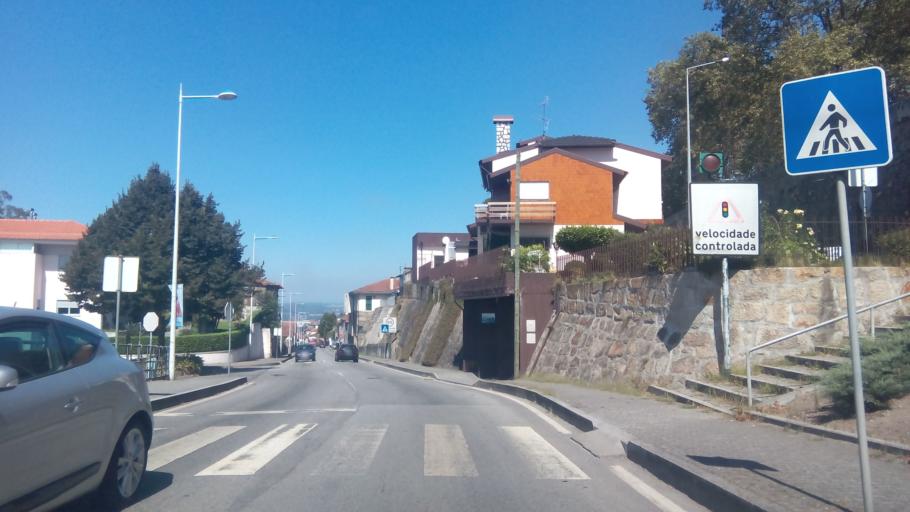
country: PT
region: Porto
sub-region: Penafiel
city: Penafiel
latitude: 41.2029
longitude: -8.2898
